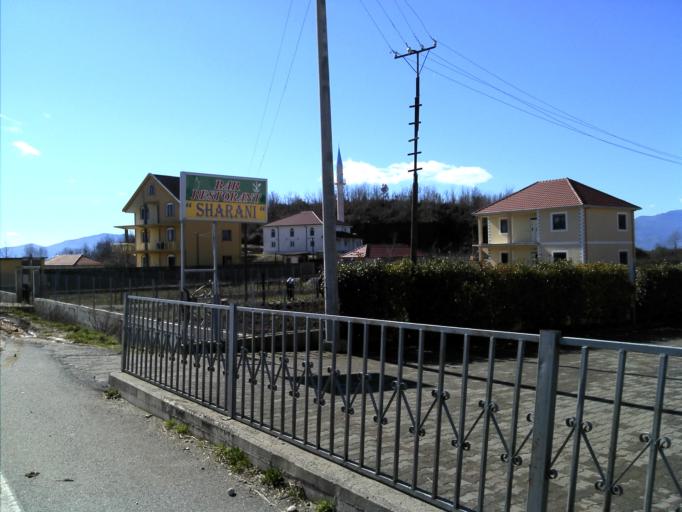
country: AL
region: Shkoder
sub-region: Rrethi i Malesia e Madhe
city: Koplik
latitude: 42.1837
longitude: 19.4593
